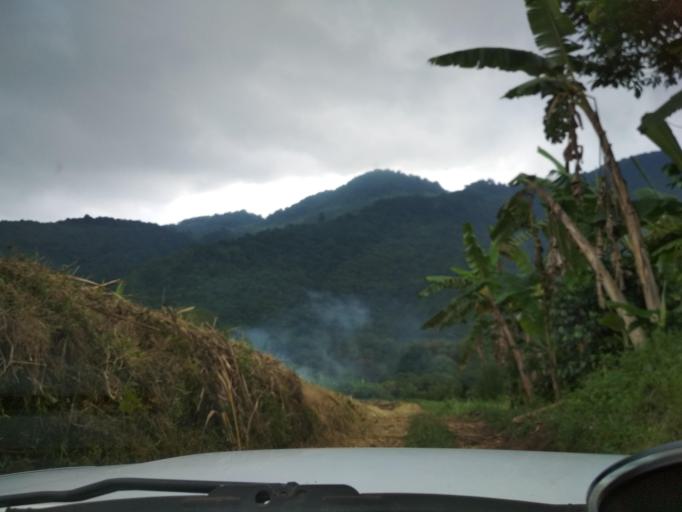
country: MX
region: Veracruz
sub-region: Fortin
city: Santa Lucia Potrerillo
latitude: 18.9553
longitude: -97.0481
